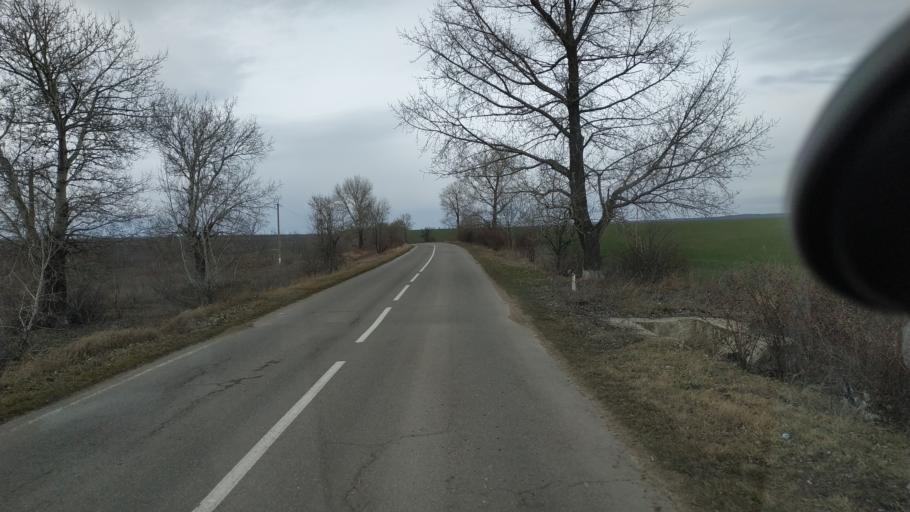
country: MD
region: Telenesti
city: Cocieri
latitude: 47.3598
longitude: 29.1158
